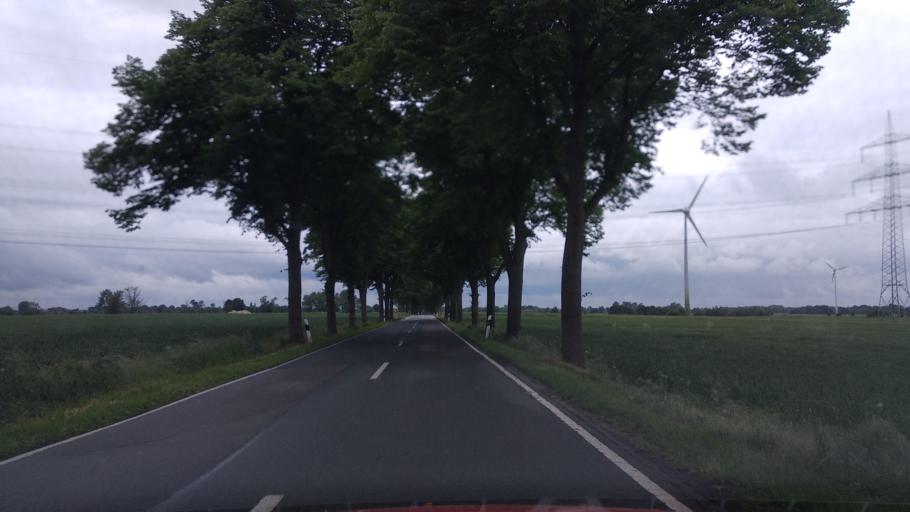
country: DE
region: Lower Saxony
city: Lindhorst
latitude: 52.3772
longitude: 9.2700
